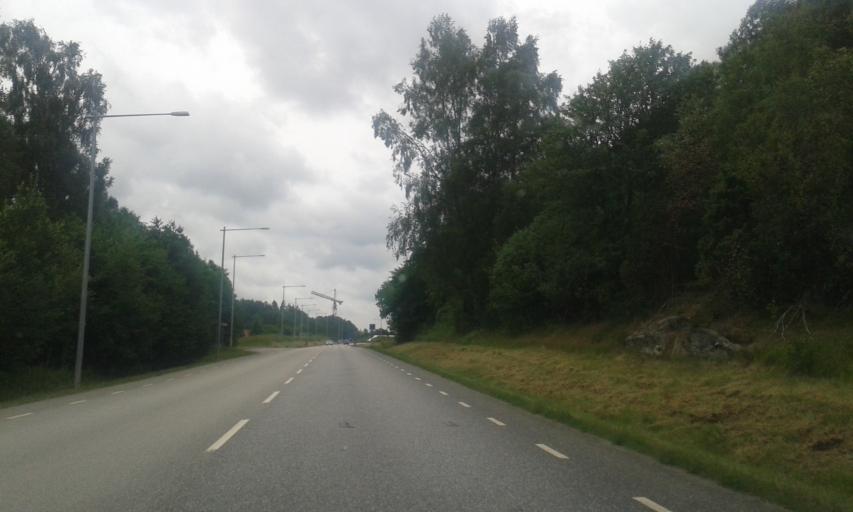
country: SE
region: Vaestra Goetaland
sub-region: Kungalvs Kommun
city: Kungalv
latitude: 57.8658
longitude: 11.8984
